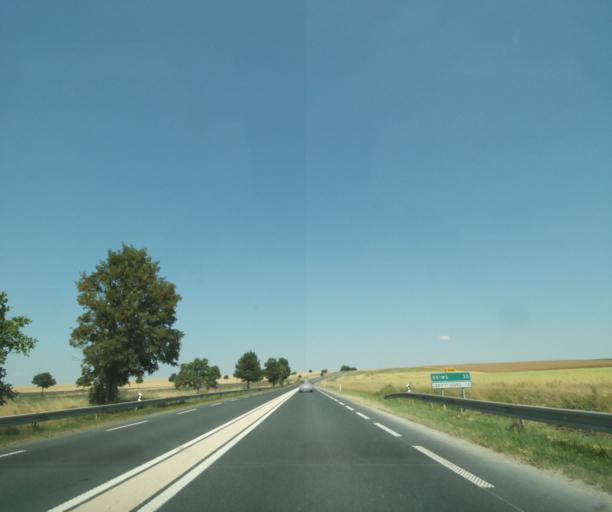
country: FR
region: Champagne-Ardenne
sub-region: Departement de la Marne
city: Mourmelon-le-Grand
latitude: 49.0708
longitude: 4.2927
